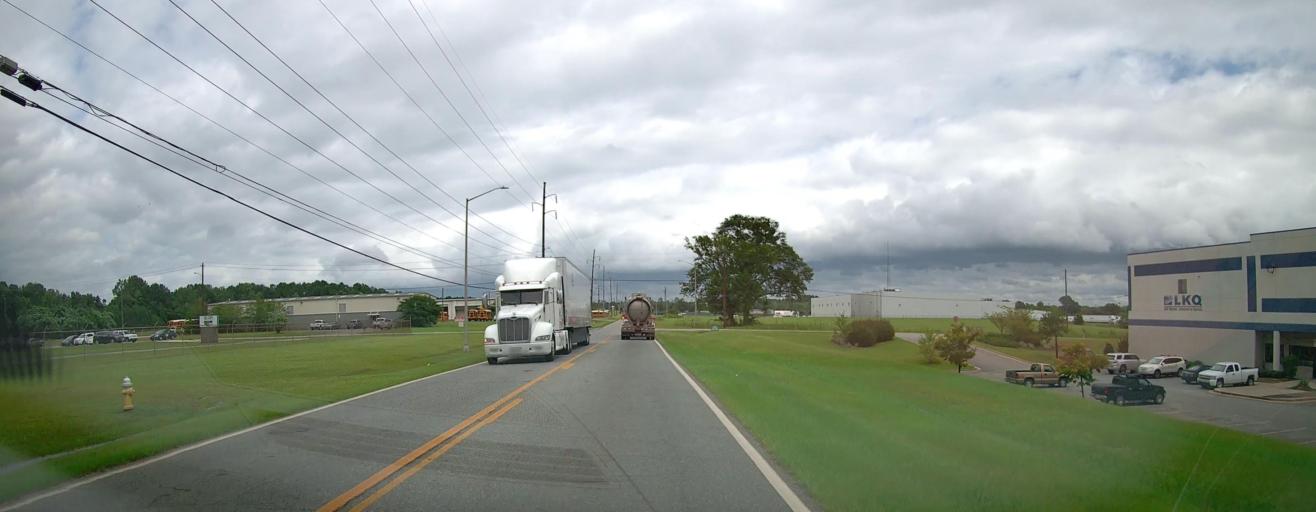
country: US
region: Georgia
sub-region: Bibb County
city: Macon
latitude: 32.8027
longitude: -83.5556
